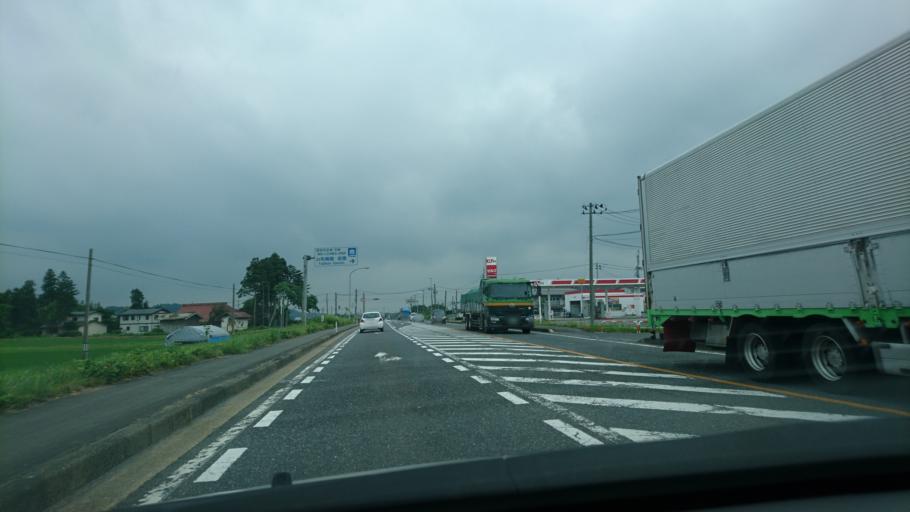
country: JP
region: Miyagi
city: Furukawa
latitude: 38.6676
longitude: 140.8684
